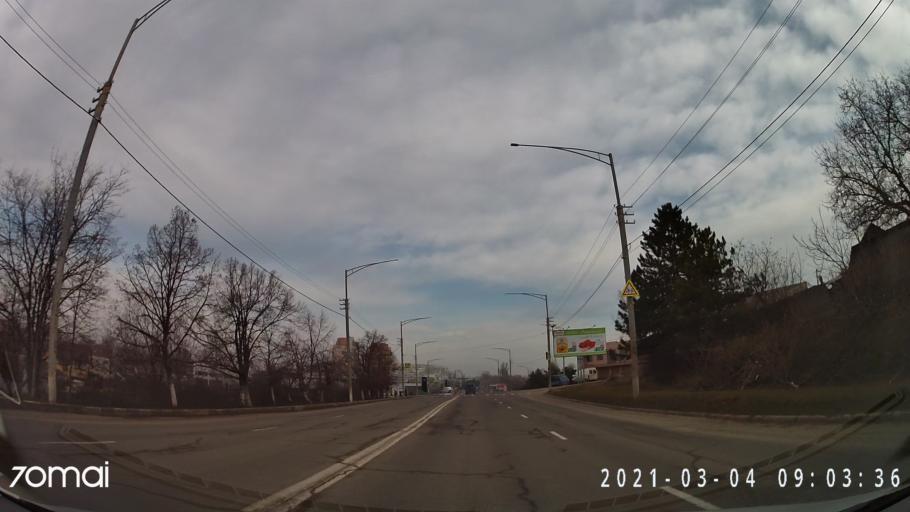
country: MD
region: Balti
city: Balti
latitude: 47.7513
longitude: 27.9436
